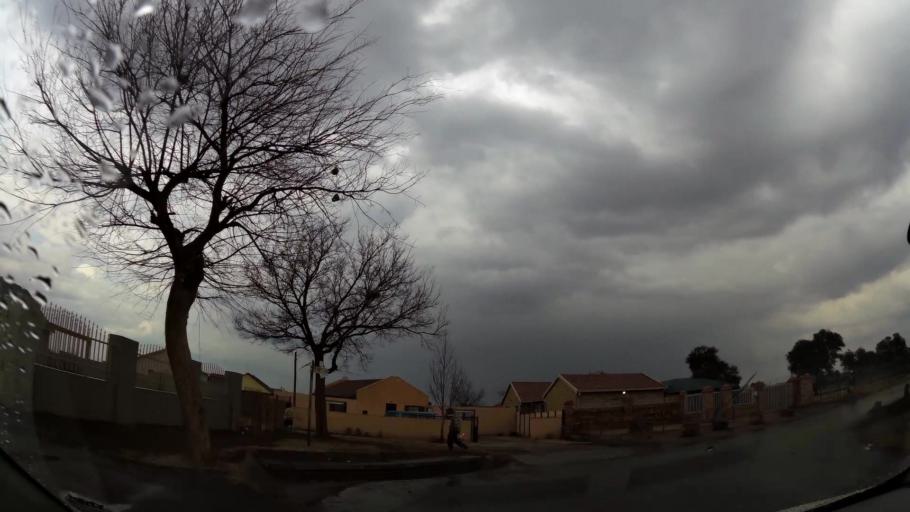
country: ZA
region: Gauteng
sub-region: Ekurhuleni Metropolitan Municipality
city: Germiston
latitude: -26.3767
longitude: 28.1342
